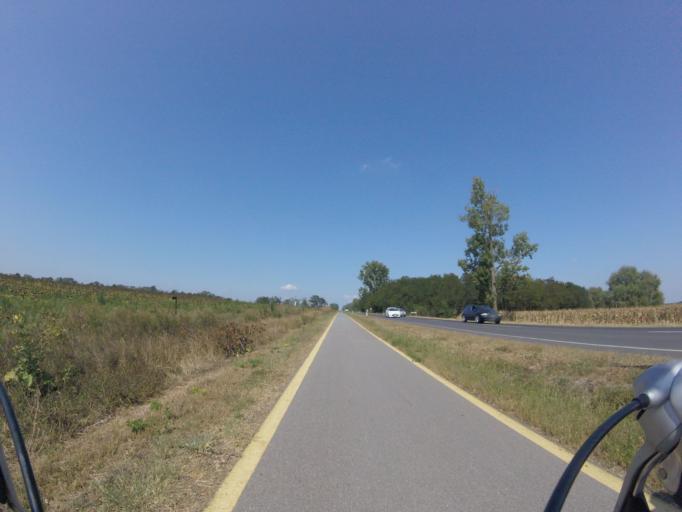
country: HU
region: Szabolcs-Szatmar-Bereg
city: Nyirtelek
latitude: 48.0268
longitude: 21.6061
